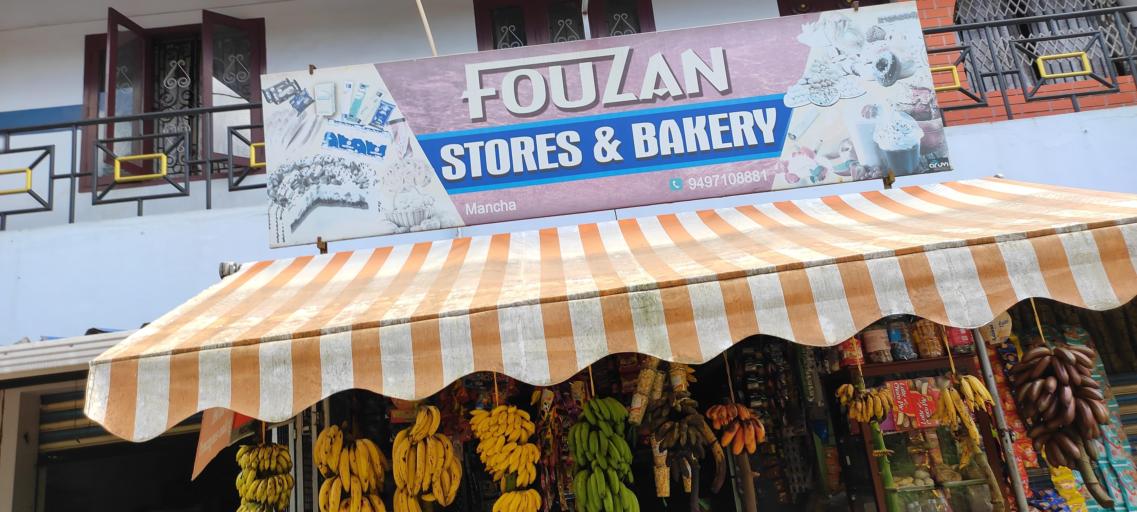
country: IN
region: Kerala
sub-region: Thiruvananthapuram
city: Nedumangad
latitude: 8.5975
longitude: 77.0083
